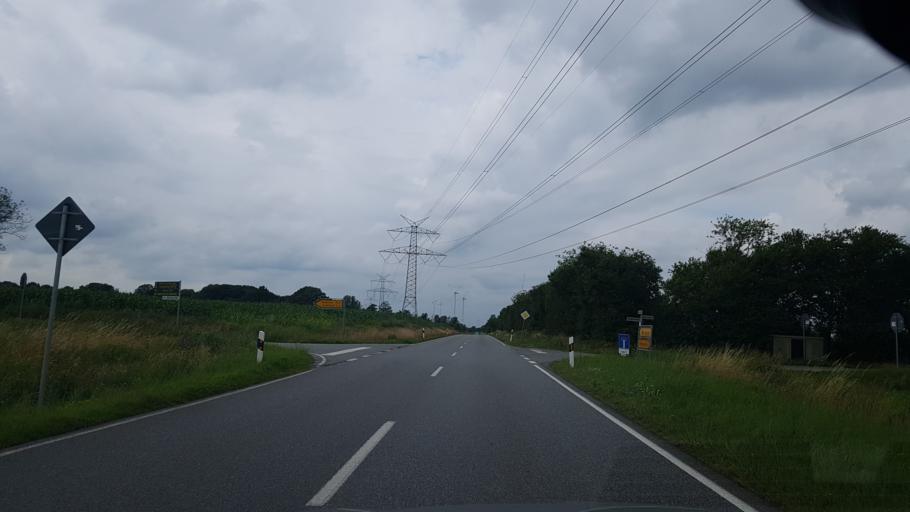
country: DE
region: Schleswig-Holstein
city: Jardelund
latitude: 54.8303
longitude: 9.2167
